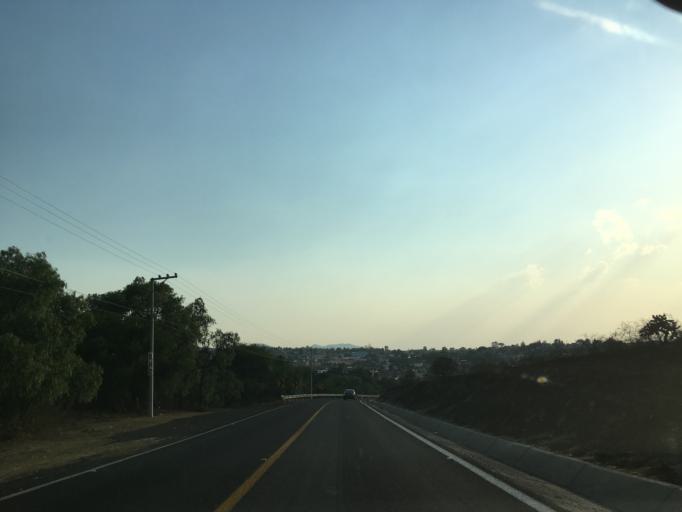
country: MX
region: Michoacan
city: Charo
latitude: 19.7556
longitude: -101.0395
